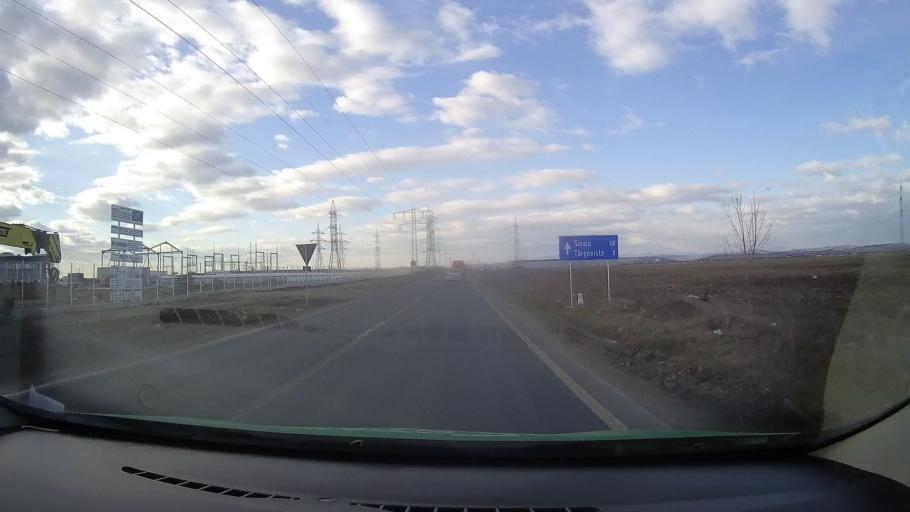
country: RO
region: Dambovita
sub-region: Comuna Ulmi
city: Ulmi
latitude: 44.8766
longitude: 25.5186
